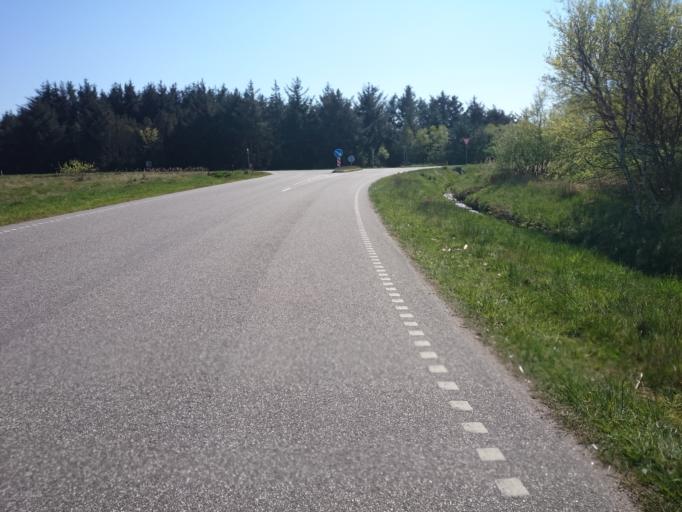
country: DK
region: North Denmark
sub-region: Frederikshavn Kommune
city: Skagen
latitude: 57.7385
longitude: 10.6017
